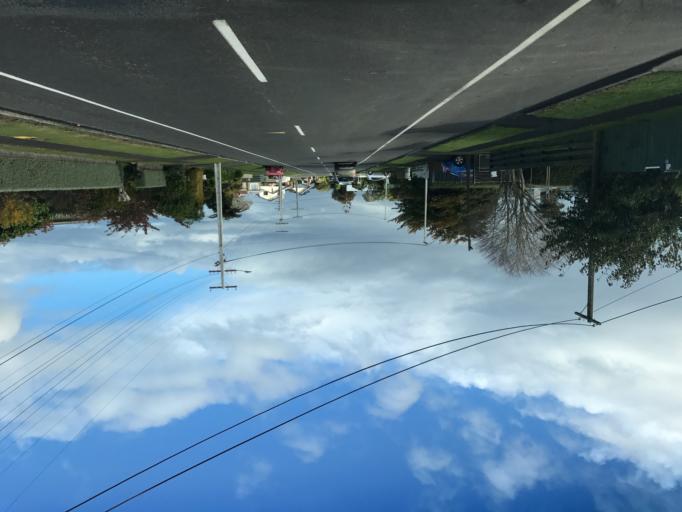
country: NZ
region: Taranaki
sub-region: South Taranaki District
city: Hawera
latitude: -39.5765
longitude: 174.2695
